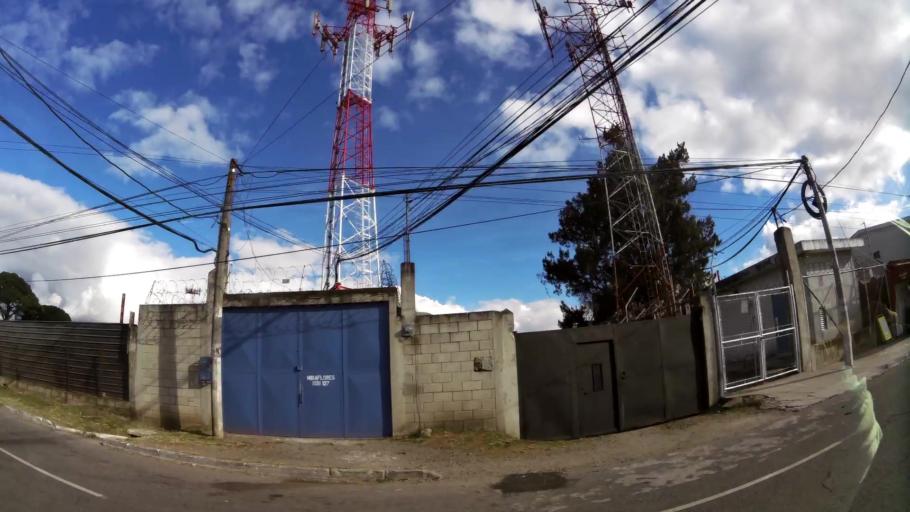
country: GT
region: Guatemala
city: Guatemala City
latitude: 14.6204
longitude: -90.5505
